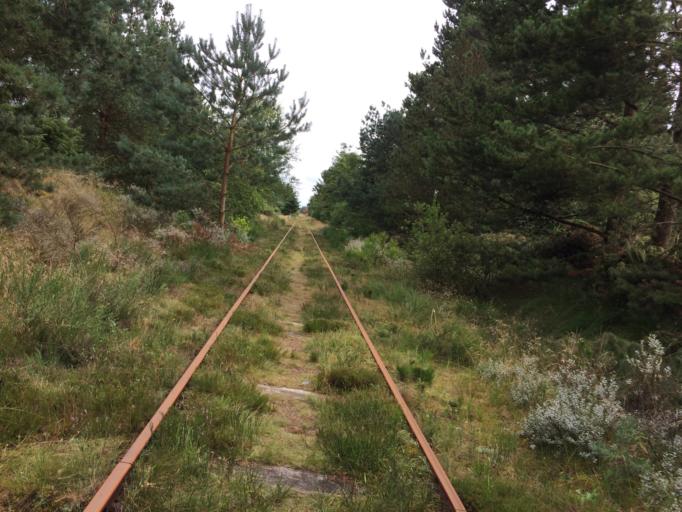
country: DK
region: South Denmark
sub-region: Varde Kommune
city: Oksbol
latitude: 55.7970
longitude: 8.2249
